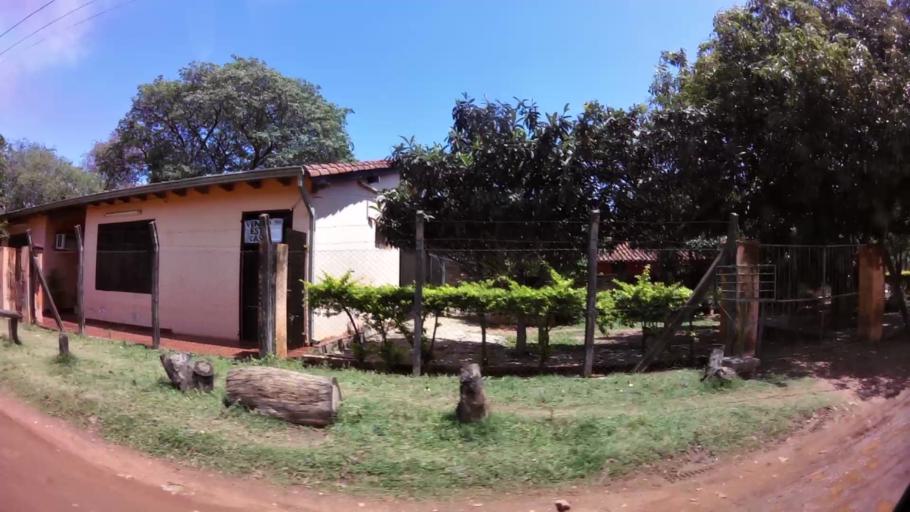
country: PY
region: Central
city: Colonia Mariano Roque Alonso
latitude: -25.2027
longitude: -57.5476
